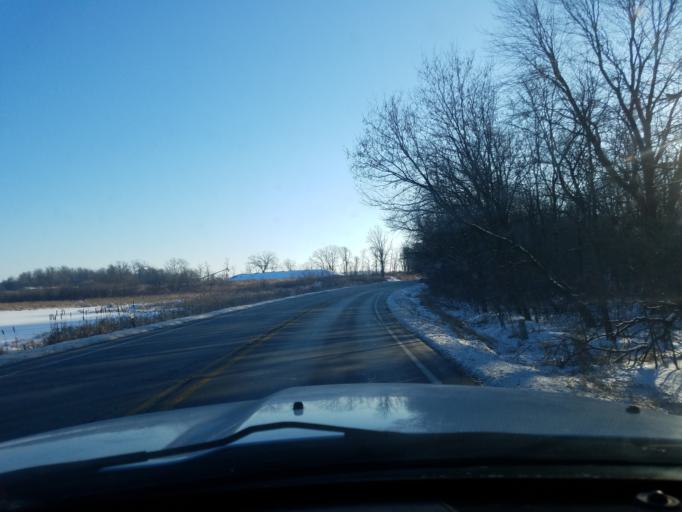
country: US
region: Indiana
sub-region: Noble County
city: Albion
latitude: 41.4568
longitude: -85.4805
